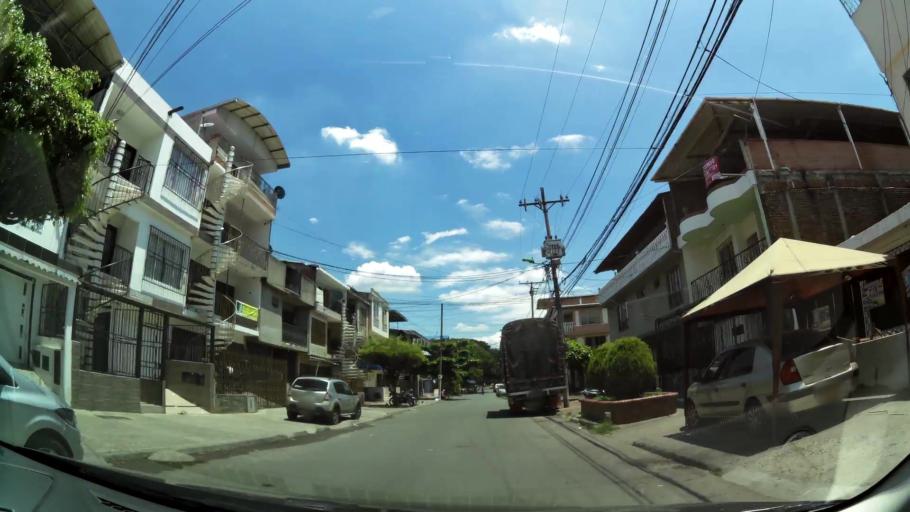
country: CO
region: Valle del Cauca
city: Cali
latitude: 3.4461
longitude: -76.4920
